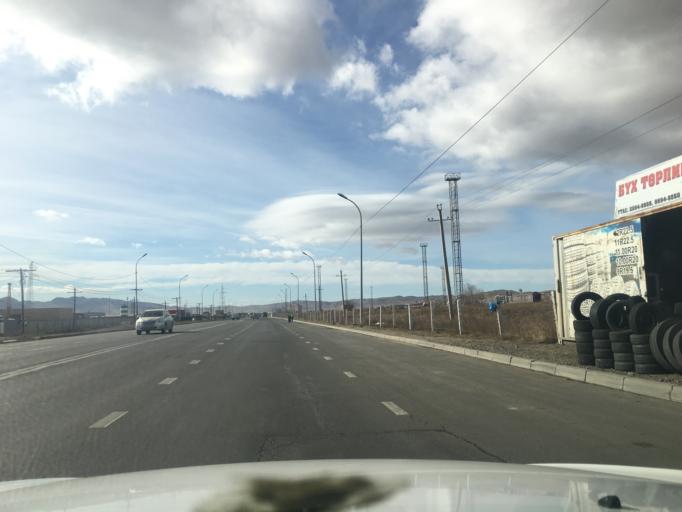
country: MN
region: Ulaanbaatar
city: Ulaanbaatar
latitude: 47.9048
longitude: 106.7566
